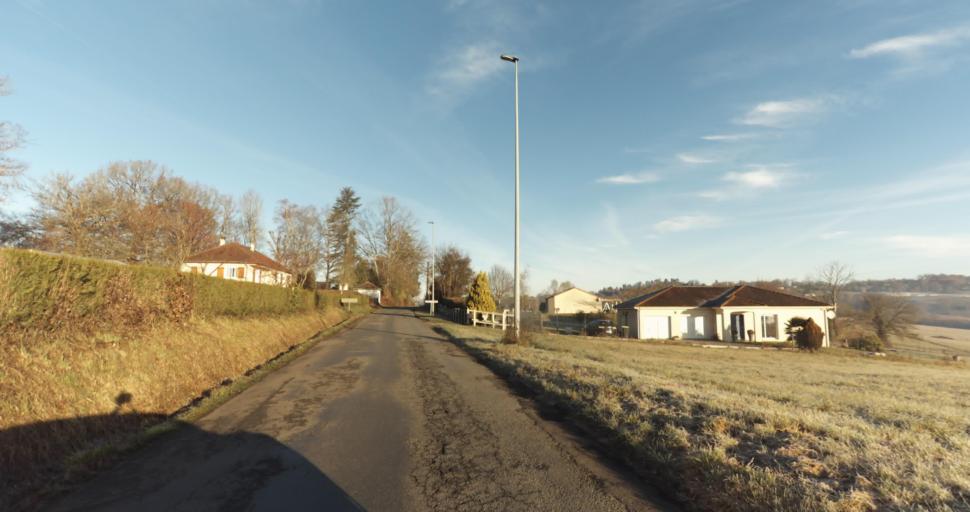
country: FR
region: Limousin
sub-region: Departement de la Haute-Vienne
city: Aixe-sur-Vienne
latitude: 45.8047
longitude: 1.1449
